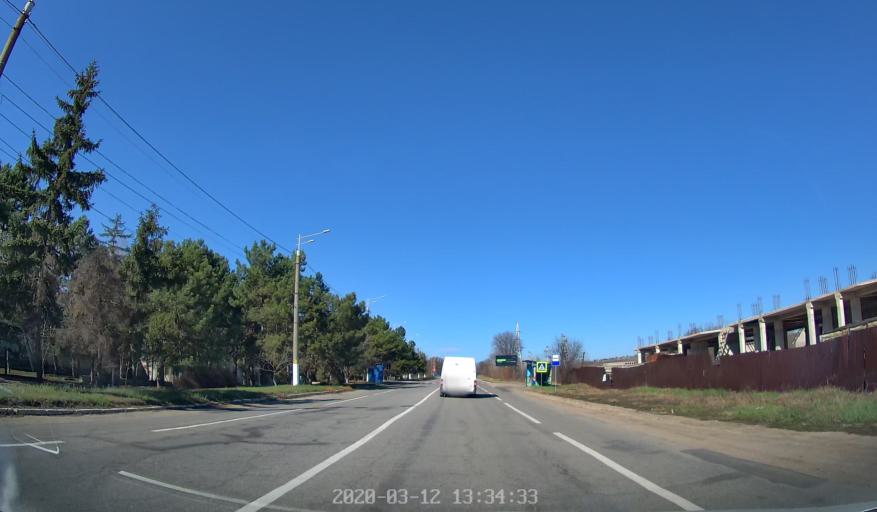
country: MD
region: Laloveni
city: Ialoveni
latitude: 46.9644
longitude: 28.7671
